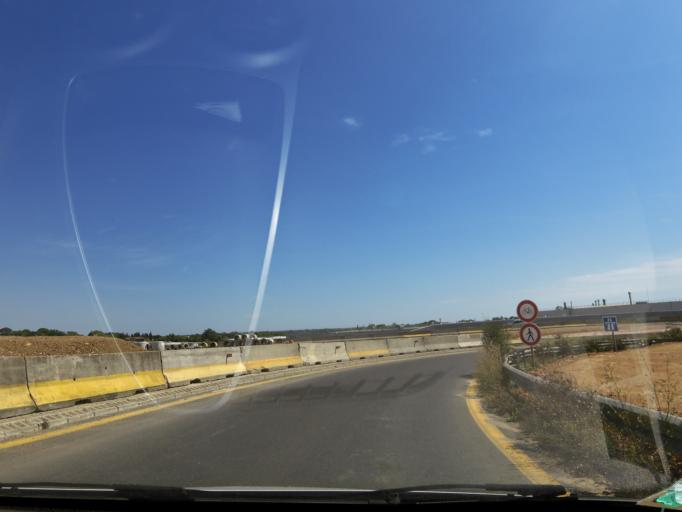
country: FR
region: Languedoc-Roussillon
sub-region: Departement de l'Herault
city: Baillargues
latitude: 43.6542
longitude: 3.9950
